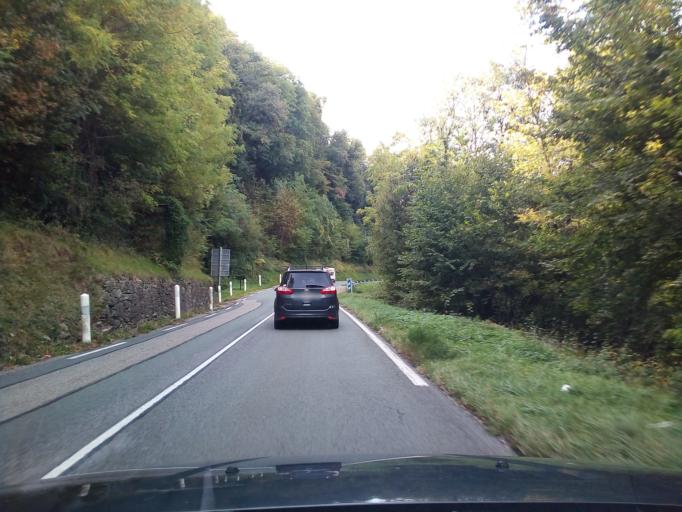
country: FR
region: Rhone-Alpes
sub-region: Departement de l'Isere
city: Goncelin
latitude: 45.3539
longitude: 5.9914
